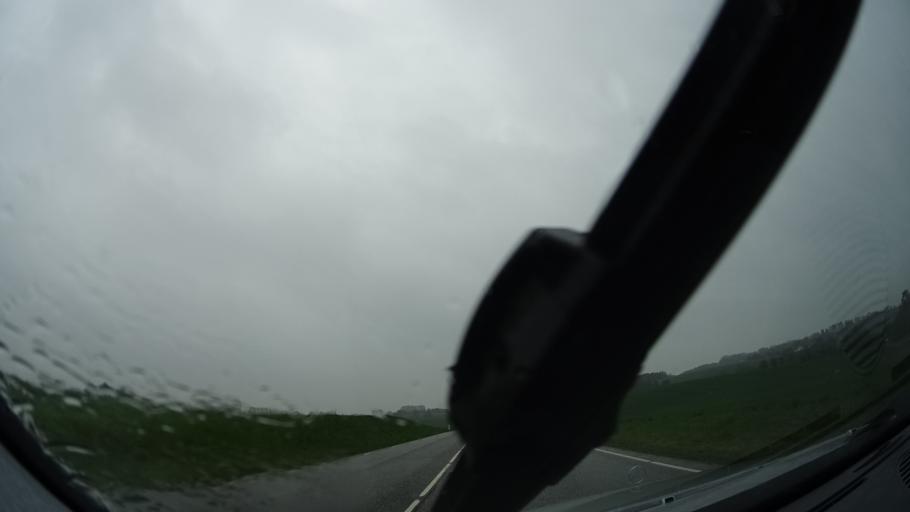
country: DK
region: Zealand
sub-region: Odsherred Kommune
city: Asnaes
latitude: 55.8212
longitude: 11.5767
